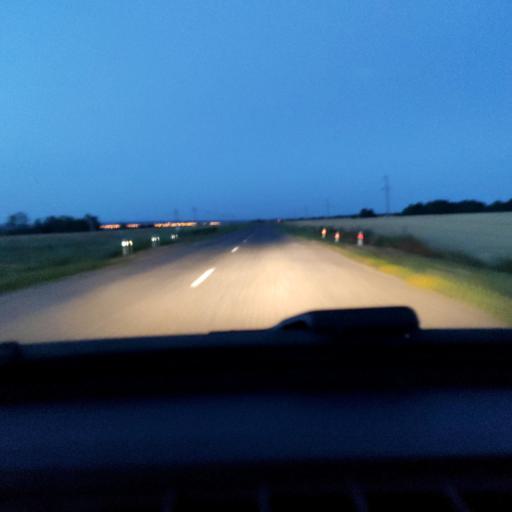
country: RU
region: Lipetsk
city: Zadonsk
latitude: 52.3104
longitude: 38.8952
